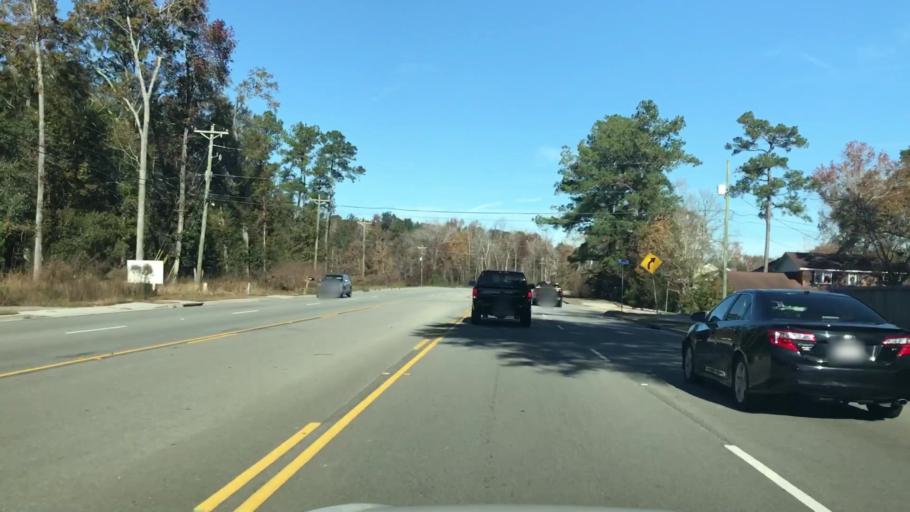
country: US
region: South Carolina
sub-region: Dorchester County
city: Centerville
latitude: 32.9626
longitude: -80.2014
